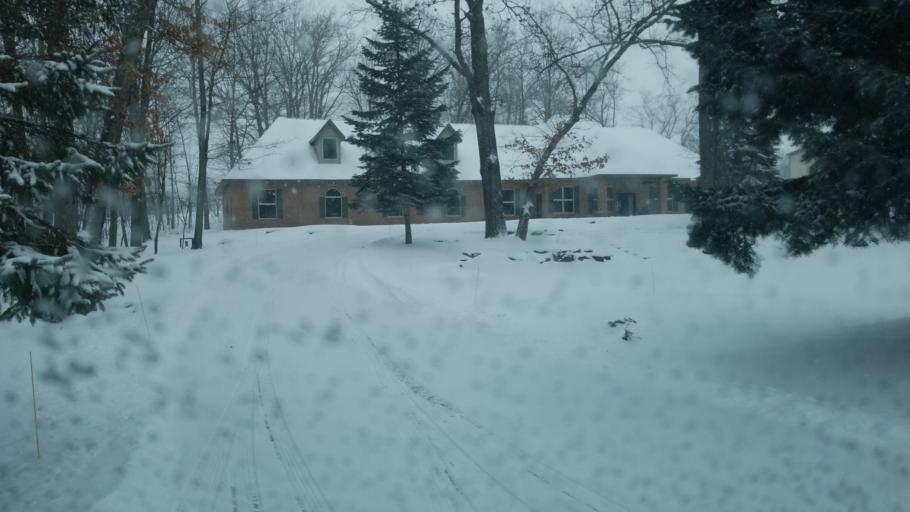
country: US
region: Michigan
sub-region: Mecosta County
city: Canadian Lakes
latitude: 43.6111
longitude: -85.3064
